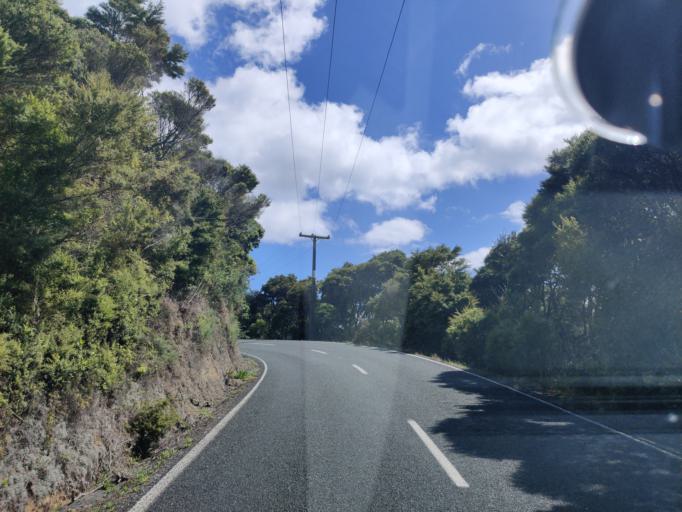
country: NZ
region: Northland
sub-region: Far North District
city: Paihia
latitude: -35.2606
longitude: 174.2458
